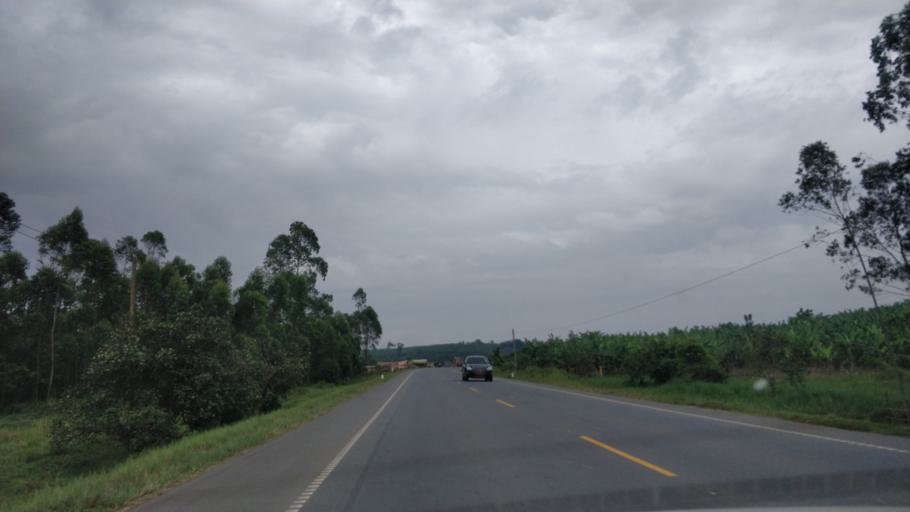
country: UG
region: Western Region
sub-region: Sheema District
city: Kibingo
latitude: -0.6519
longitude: 30.4844
